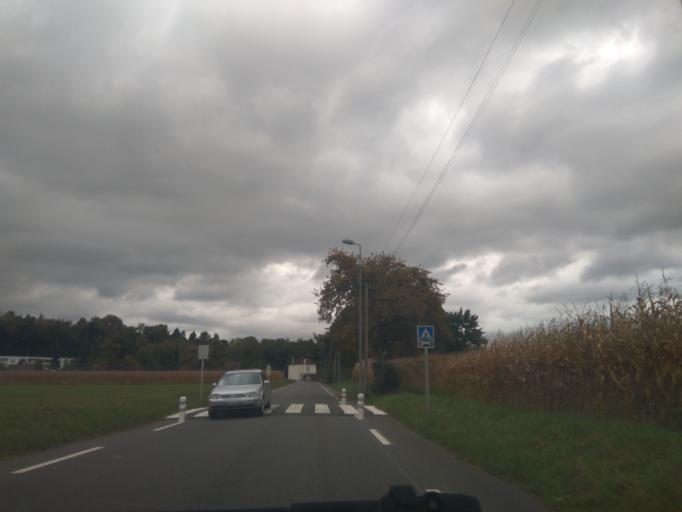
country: FR
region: Aquitaine
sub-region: Departement des Pyrenees-Atlantiques
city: Bizanos
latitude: 43.2929
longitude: -0.3378
